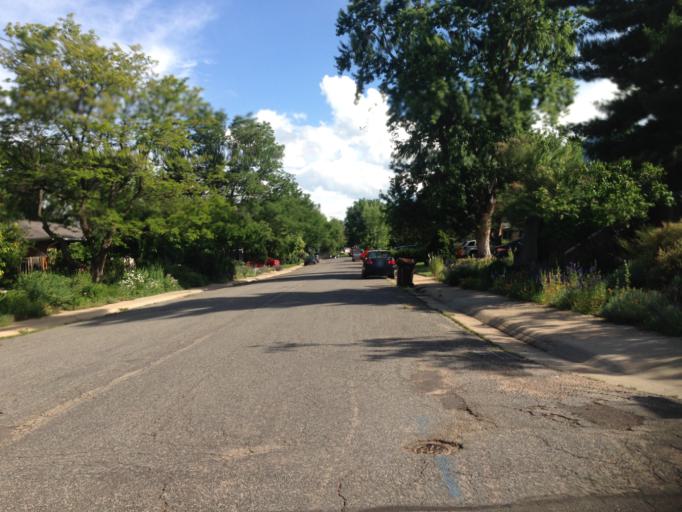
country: US
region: Colorado
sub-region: Boulder County
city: Boulder
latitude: 40.0293
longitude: -105.2750
